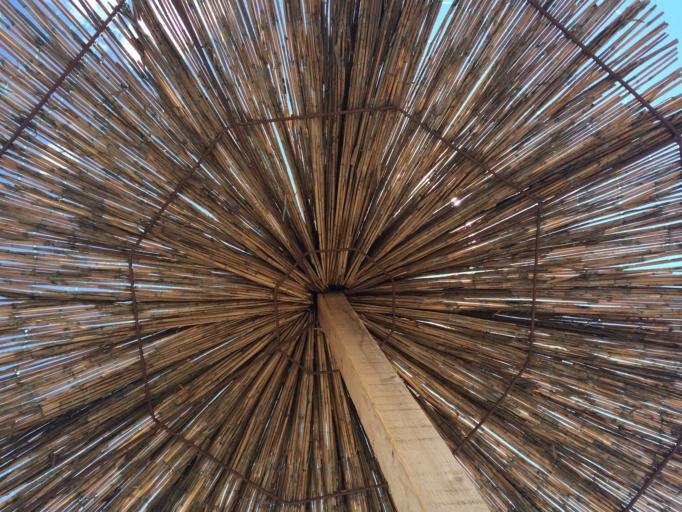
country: ME
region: Ulcinj
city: Ulcinj
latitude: 41.9094
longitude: 19.2409
